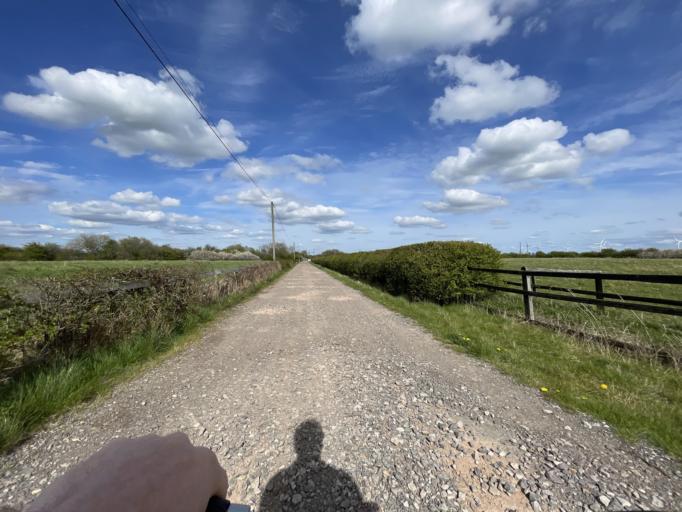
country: GB
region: England
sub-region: Warwickshire
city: Rugby
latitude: 52.3773
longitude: -1.1893
